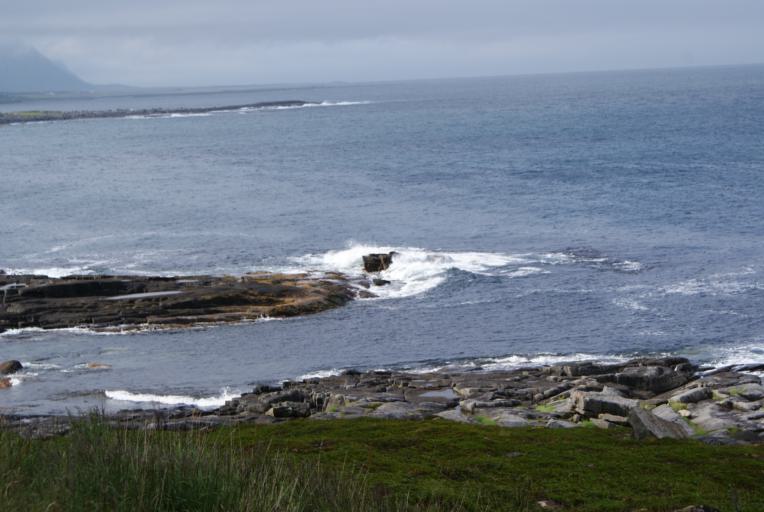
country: NO
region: Nordland
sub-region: Andoy
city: Myre
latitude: 69.0991
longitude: 15.5624
